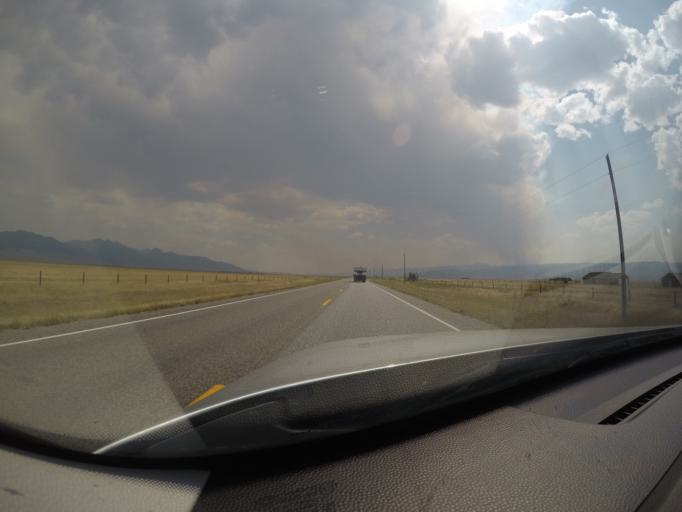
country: US
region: Montana
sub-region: Madison County
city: Virginia City
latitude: 45.1830
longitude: -111.6789
